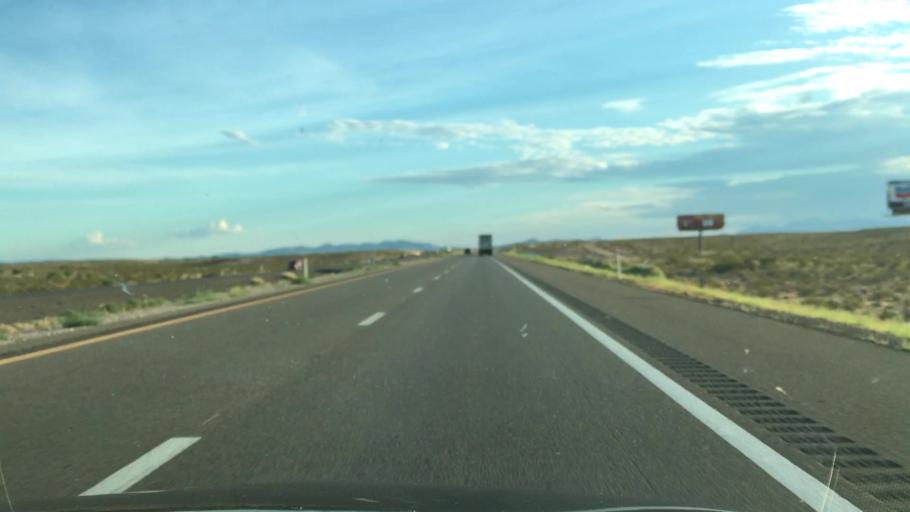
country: US
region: Nevada
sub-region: Clark County
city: Moapa Town
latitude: 36.5276
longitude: -114.7286
